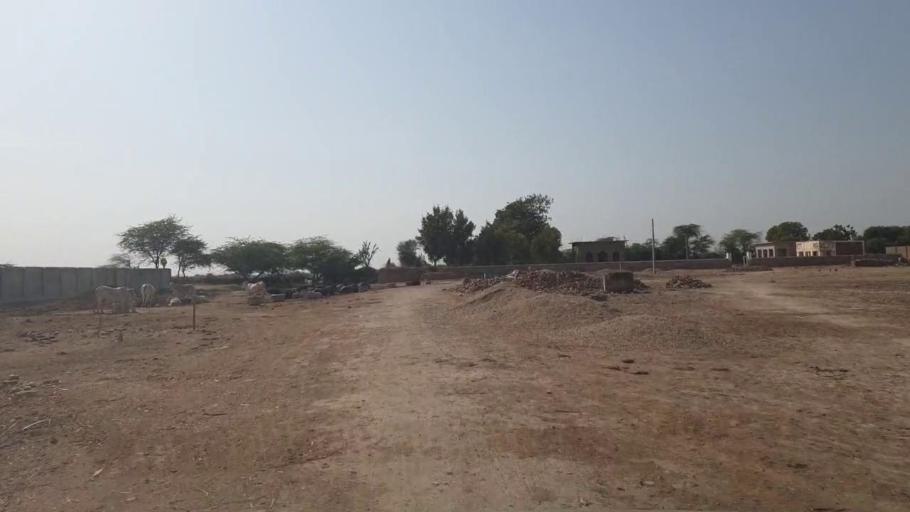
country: PK
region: Sindh
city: Dhoro Naro
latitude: 25.4448
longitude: 69.5480
